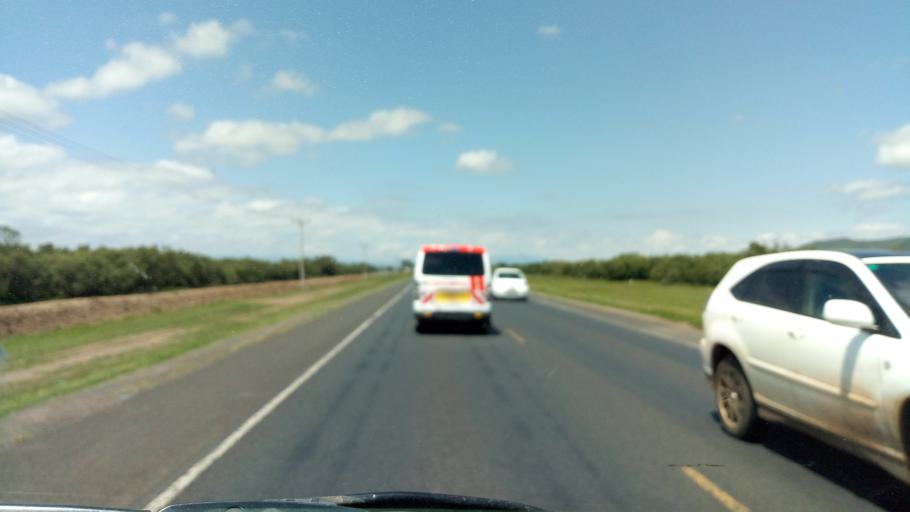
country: KE
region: Nakuru
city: Naivasha
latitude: -0.5560
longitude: 36.3505
